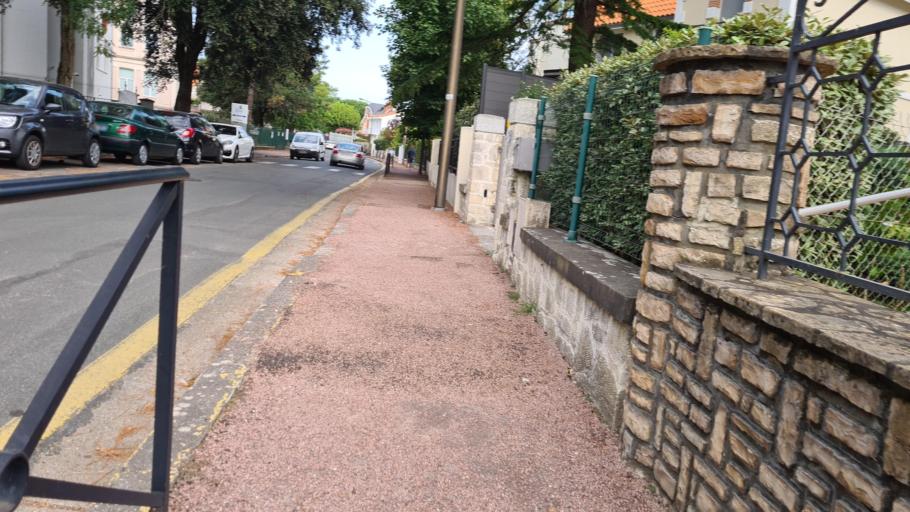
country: FR
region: Poitou-Charentes
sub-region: Departement de la Charente-Maritime
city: Saint-Georges-de-Didonne
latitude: 45.6173
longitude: -1.0104
